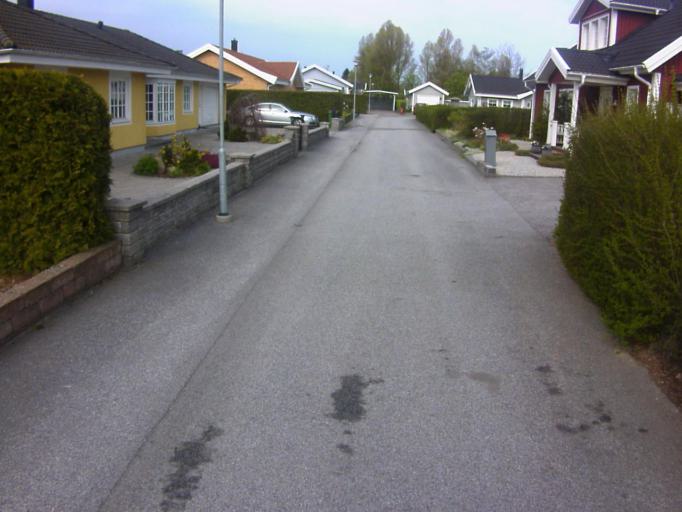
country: SE
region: Skane
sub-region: Kavlinge Kommun
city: Loddekopinge
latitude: 55.8181
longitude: 13.0207
